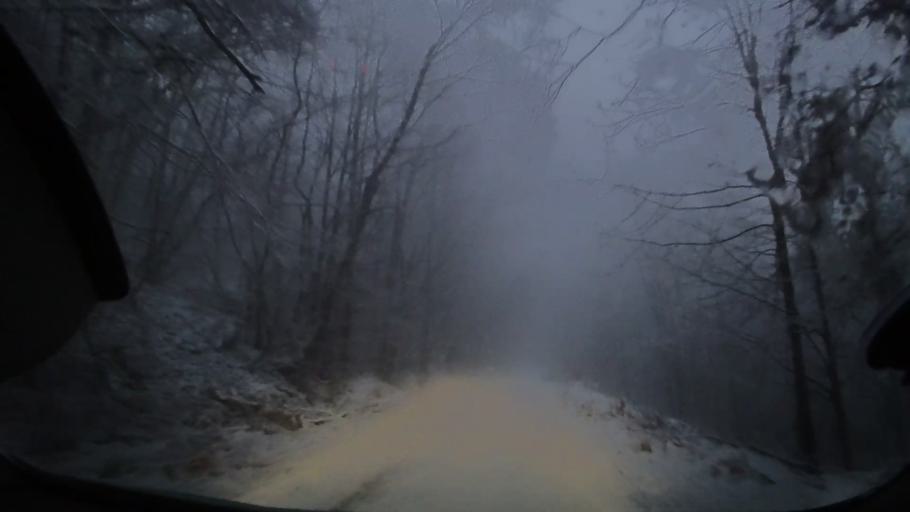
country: RO
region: Alba
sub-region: Comuna Avram Iancu
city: Avram Iancu
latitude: 46.3146
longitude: 22.8039
